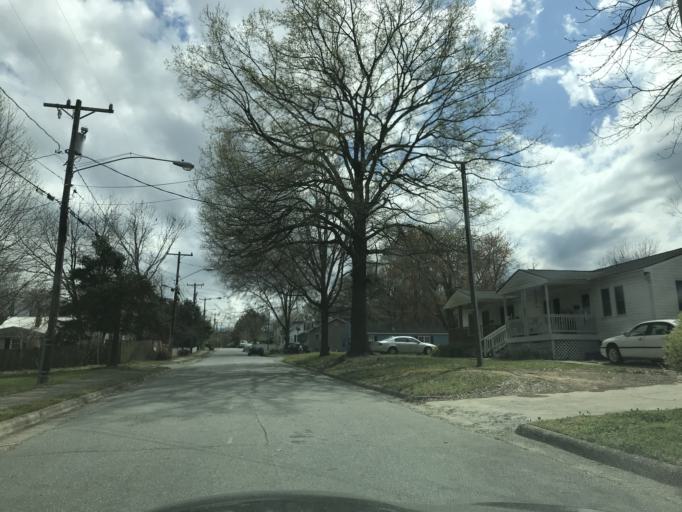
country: US
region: North Carolina
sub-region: Orange County
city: Carrboro
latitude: 35.9139
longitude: -79.0684
